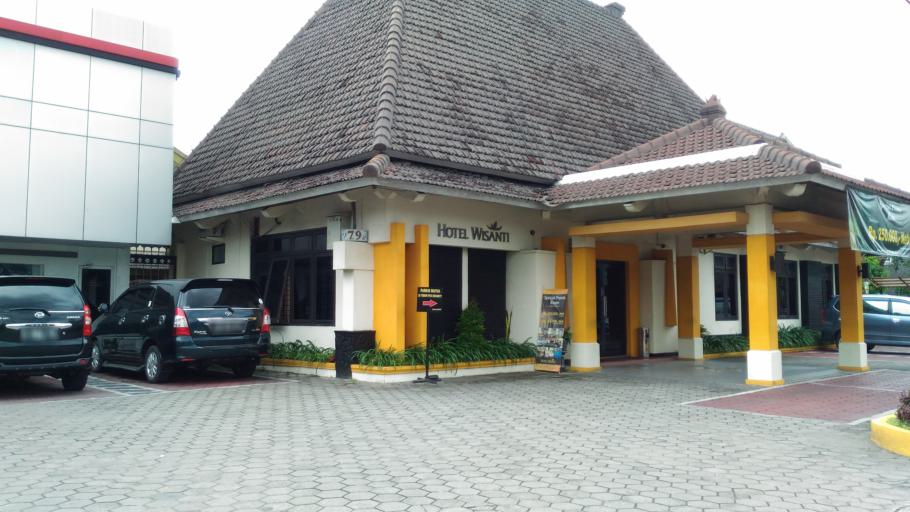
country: ID
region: Daerah Istimewa Yogyakarta
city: Yogyakarta
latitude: -7.8093
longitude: 110.3773
